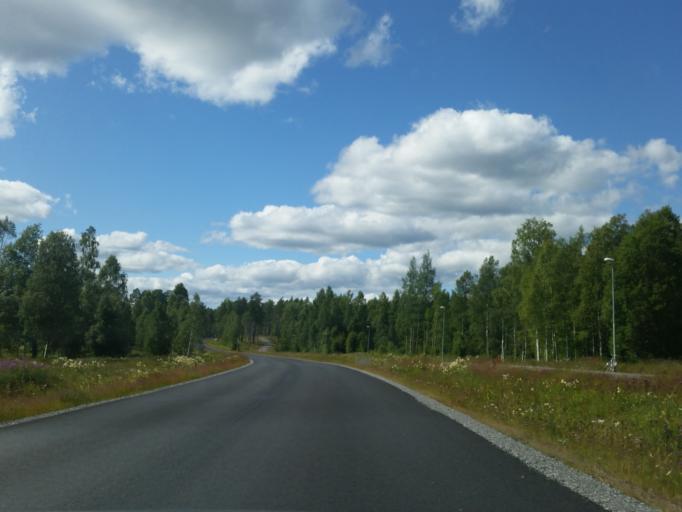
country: SE
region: Vaesterbotten
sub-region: Robertsfors Kommun
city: Robertsfors
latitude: 64.1836
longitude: 20.8784
